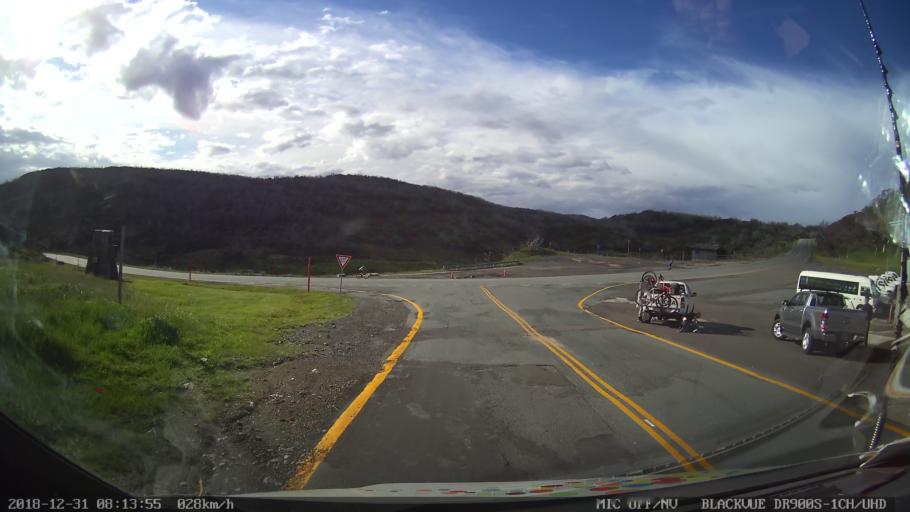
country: AU
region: New South Wales
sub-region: Snowy River
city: Jindabyne
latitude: -36.3937
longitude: 148.4278
